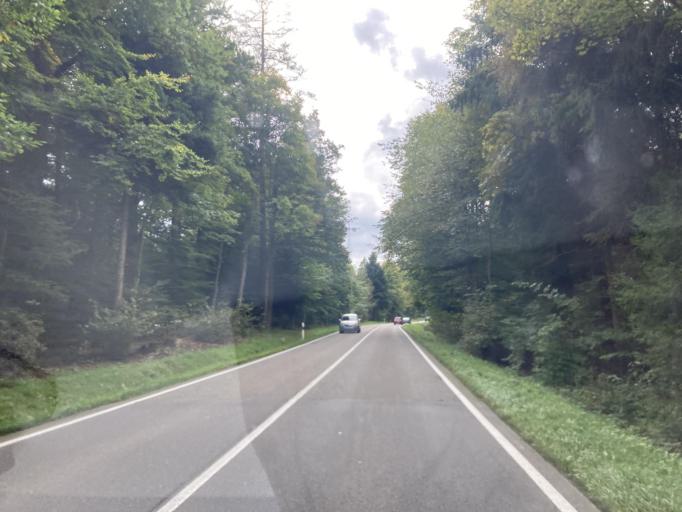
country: DE
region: Baden-Wuerttemberg
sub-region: Karlsruhe Region
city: Birkenfeld
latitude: 48.8648
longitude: 8.6178
